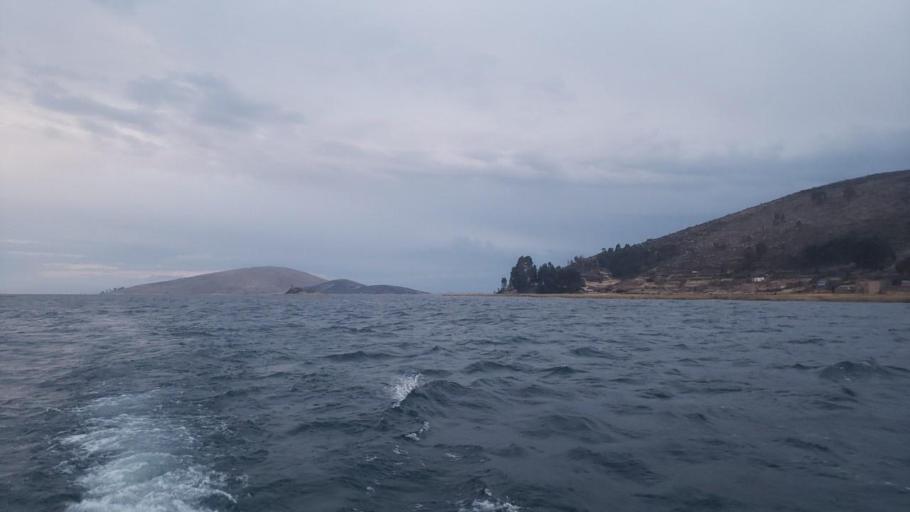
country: BO
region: La Paz
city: San Pablo
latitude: -16.2368
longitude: -68.8296
